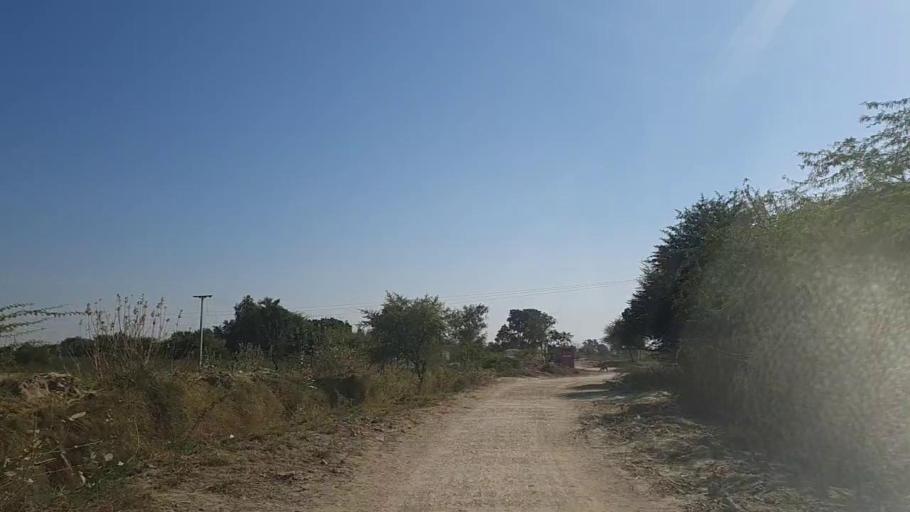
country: PK
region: Sindh
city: Kunri
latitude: 25.2314
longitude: 69.4843
